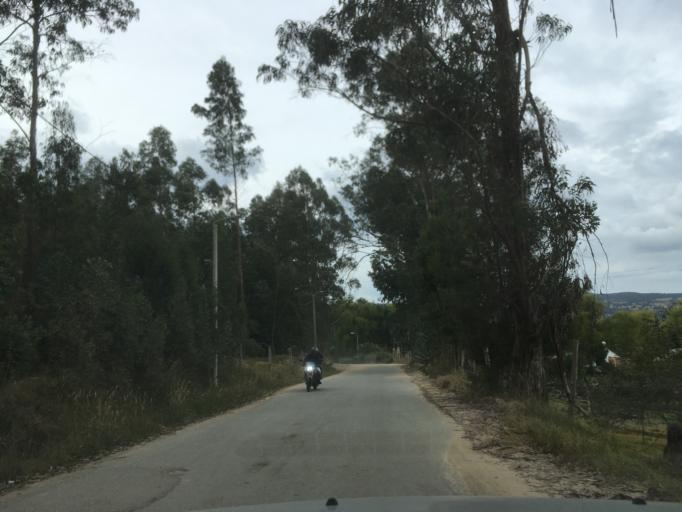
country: CO
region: Boyaca
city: Firavitoba
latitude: 5.6733
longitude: -73.0027
